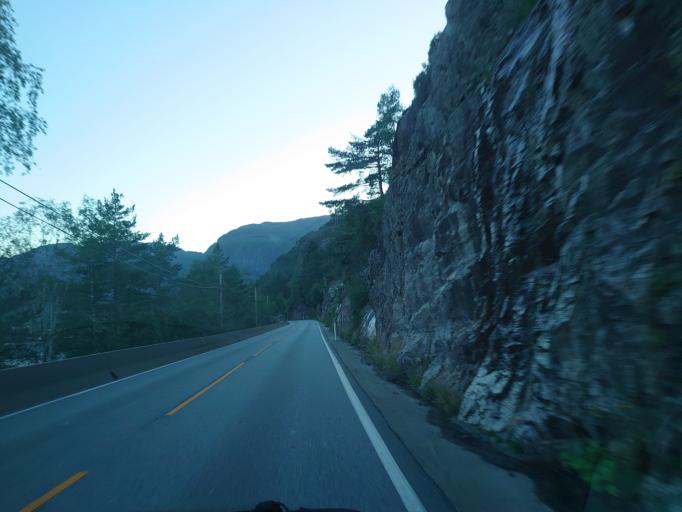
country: NO
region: Hordaland
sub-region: Osteroy
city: Lonevag
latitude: 60.7036
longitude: 5.6042
